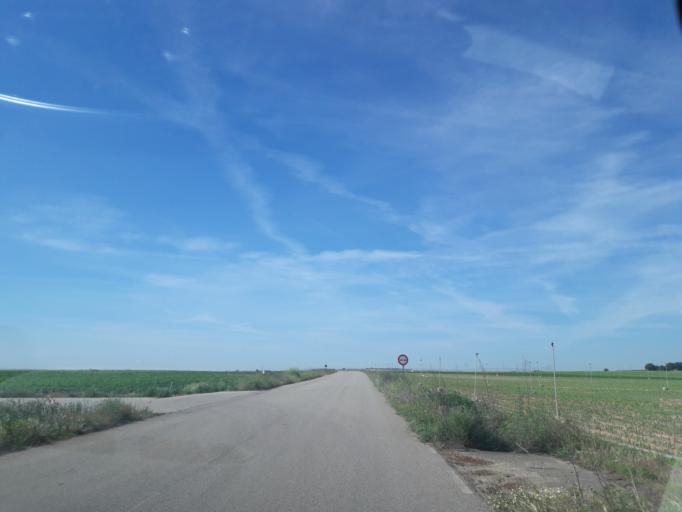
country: ES
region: Castille and Leon
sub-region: Provincia de Salamanca
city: Villoruela
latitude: 41.0347
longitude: -5.3896
